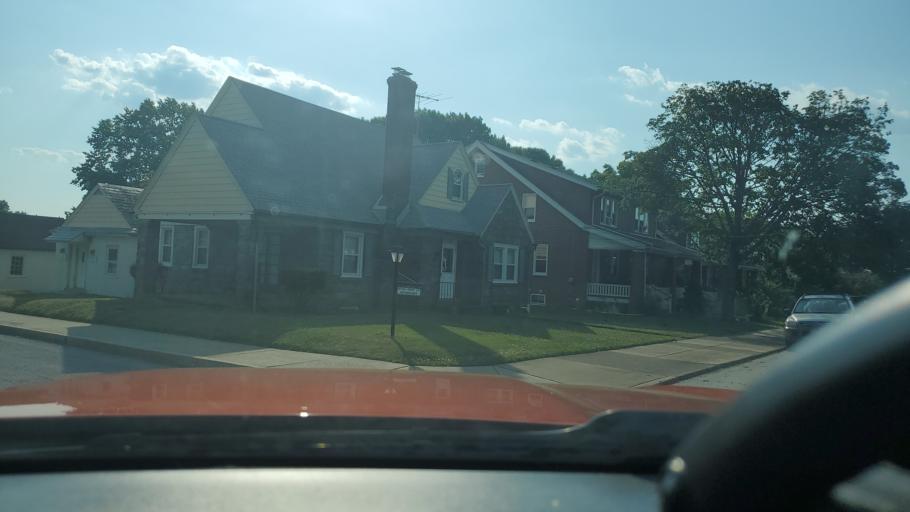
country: US
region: Pennsylvania
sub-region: Montgomery County
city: Souderton
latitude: 40.3057
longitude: -75.3183
